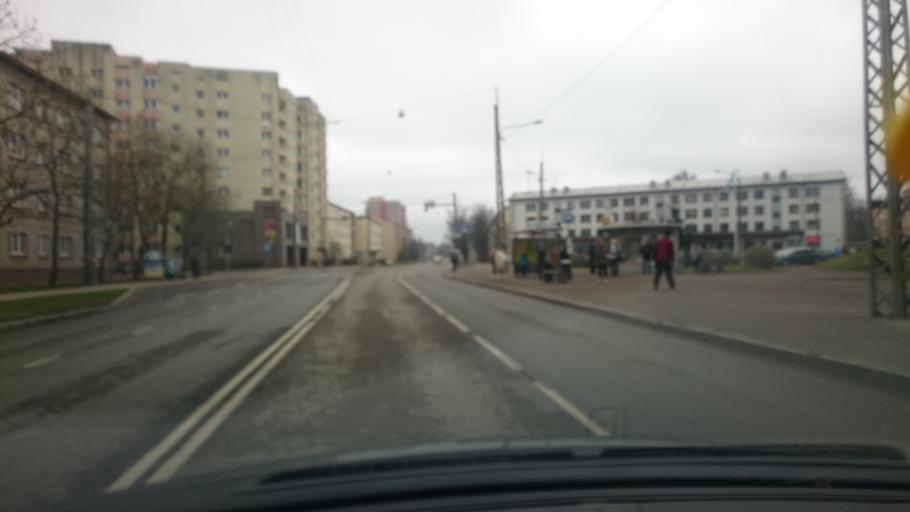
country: EE
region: Harju
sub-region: Tallinna linn
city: Tallinn
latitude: 59.4495
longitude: 24.6974
